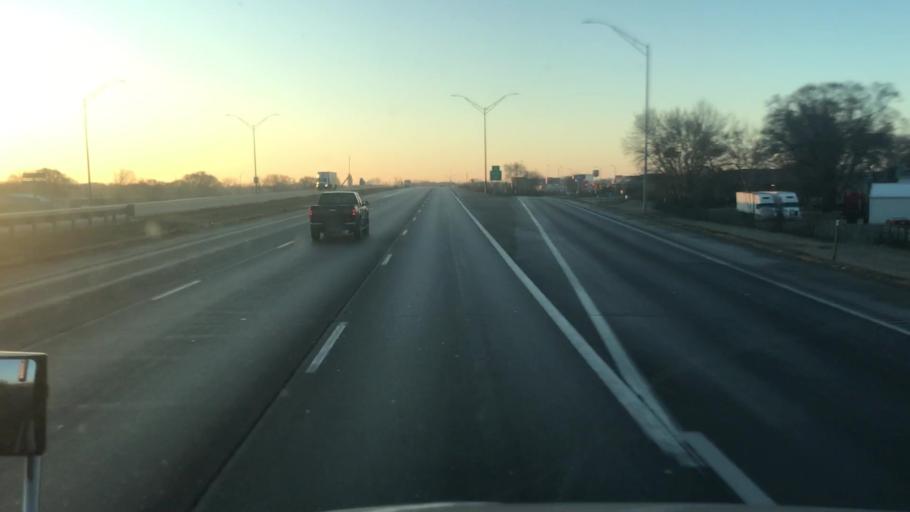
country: US
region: Iowa
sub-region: Black Hawk County
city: Waterloo
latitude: 42.4717
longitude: -92.3210
